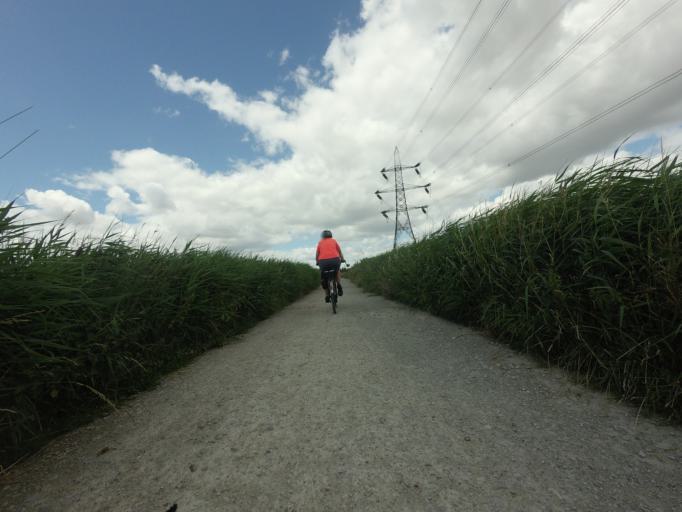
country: GB
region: England
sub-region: Kent
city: Gravesend
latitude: 51.4394
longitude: 0.4135
